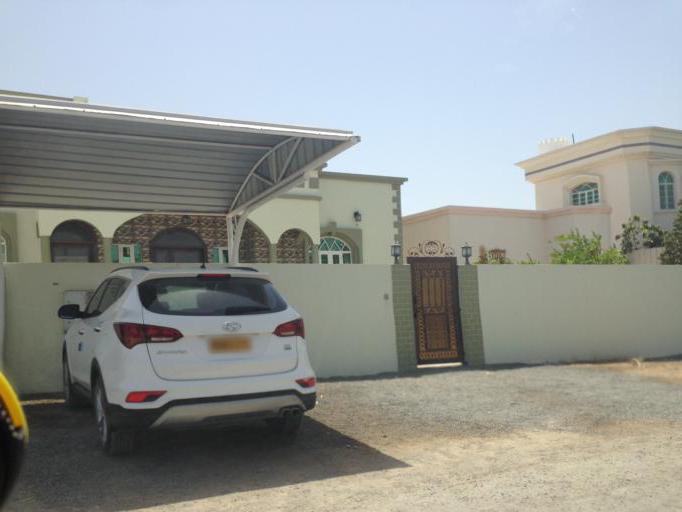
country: OM
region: Muhafazat Masqat
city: As Sib al Jadidah
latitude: 23.6877
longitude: 58.1129
